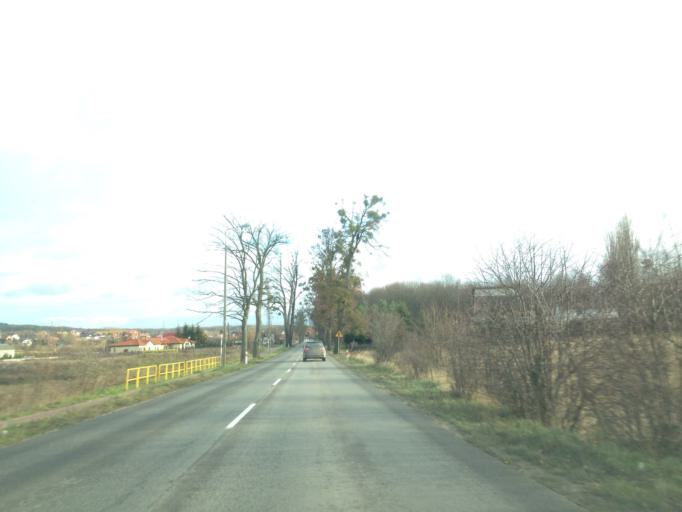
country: PL
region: Pomeranian Voivodeship
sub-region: Powiat gdanski
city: Kolbudy
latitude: 54.2779
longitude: 18.4807
